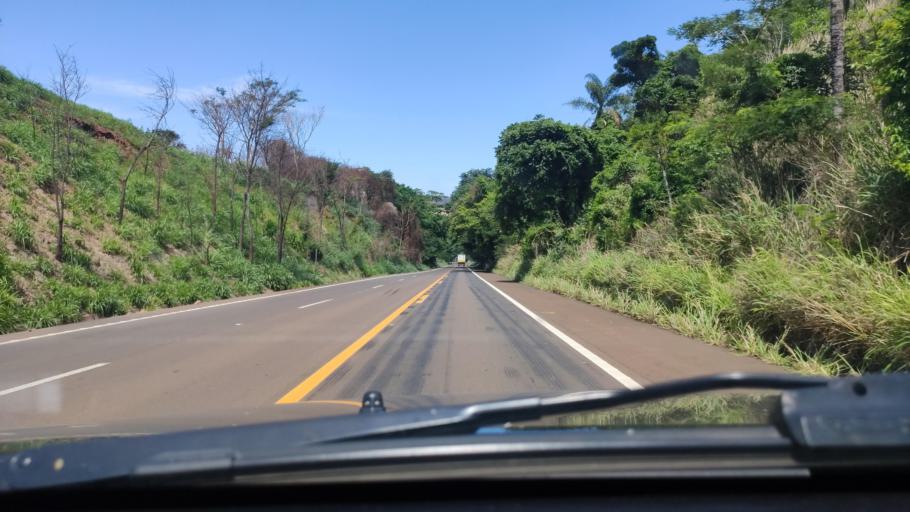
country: BR
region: Sao Paulo
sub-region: Ribeirao Bonito
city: Ribeirao Bonito
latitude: -22.0608
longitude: -48.0844
